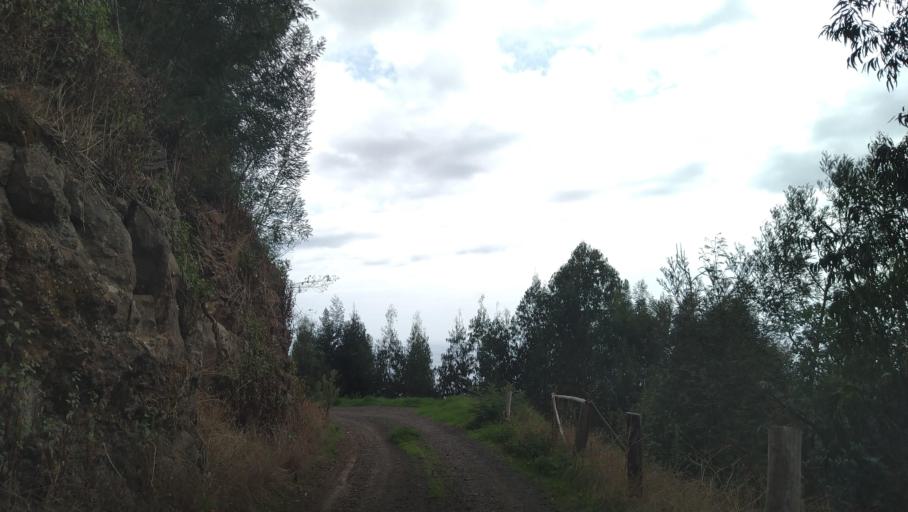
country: PT
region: Madeira
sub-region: Funchal
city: Nossa Senhora do Monte
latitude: 32.6815
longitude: -16.9238
